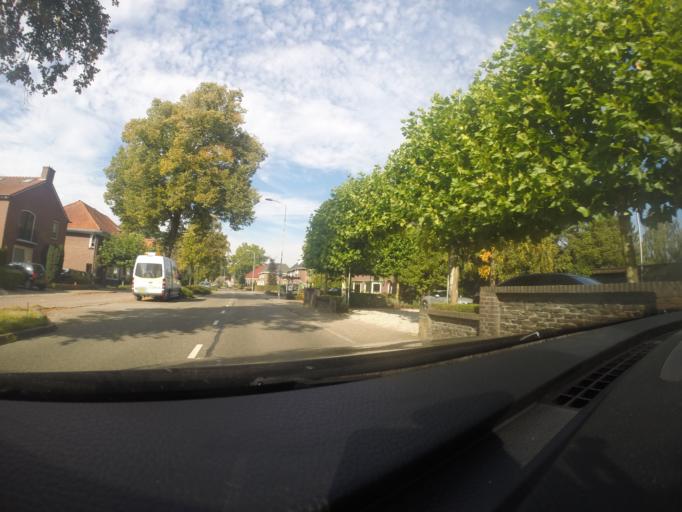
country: NL
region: Gelderland
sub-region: Oude IJsselstreek
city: Gendringen
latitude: 51.9234
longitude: 6.3607
